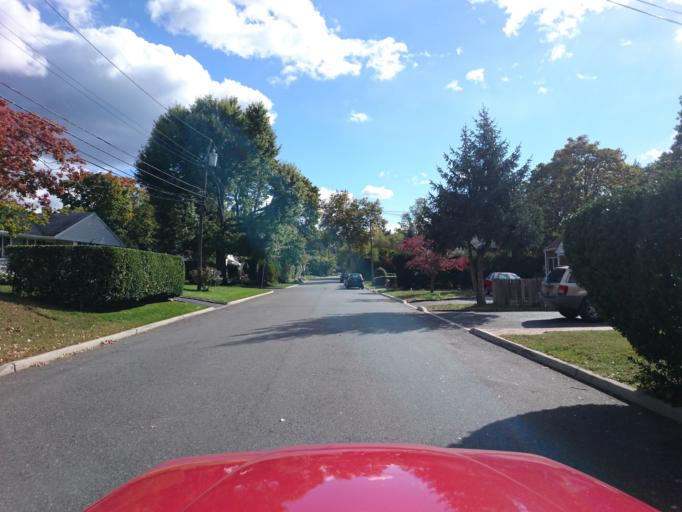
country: US
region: New York
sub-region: Nassau County
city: Glen Cove
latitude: 40.8603
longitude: -73.6302
